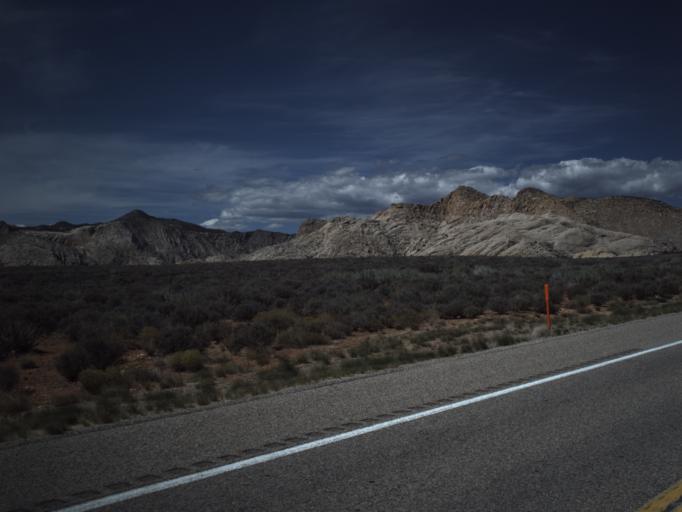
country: US
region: Utah
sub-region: Washington County
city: Ivins
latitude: 37.2194
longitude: -113.6333
